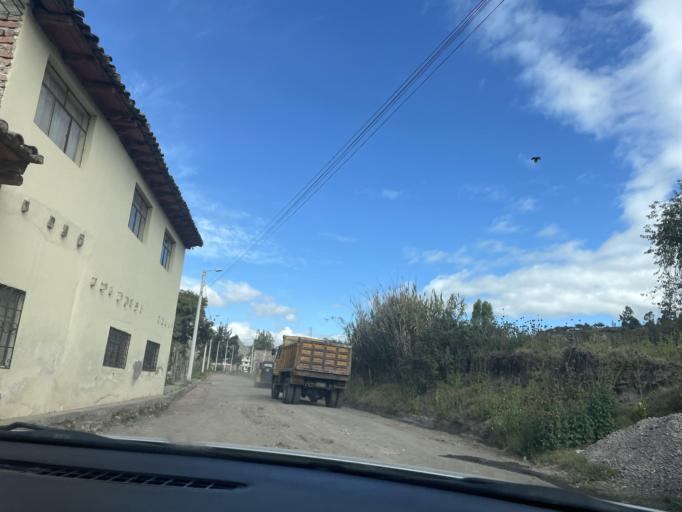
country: EC
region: Chimborazo
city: Guano
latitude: -1.6056
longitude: -78.6235
